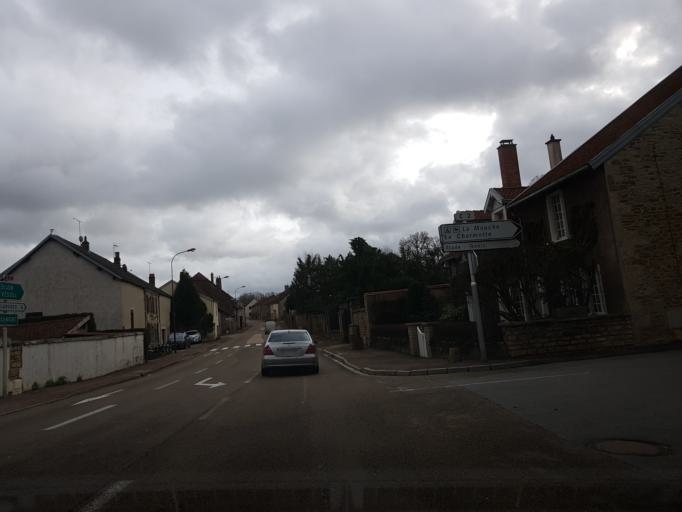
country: FR
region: Champagne-Ardenne
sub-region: Departement de la Haute-Marne
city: Langres
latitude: 47.9030
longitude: 5.3034
